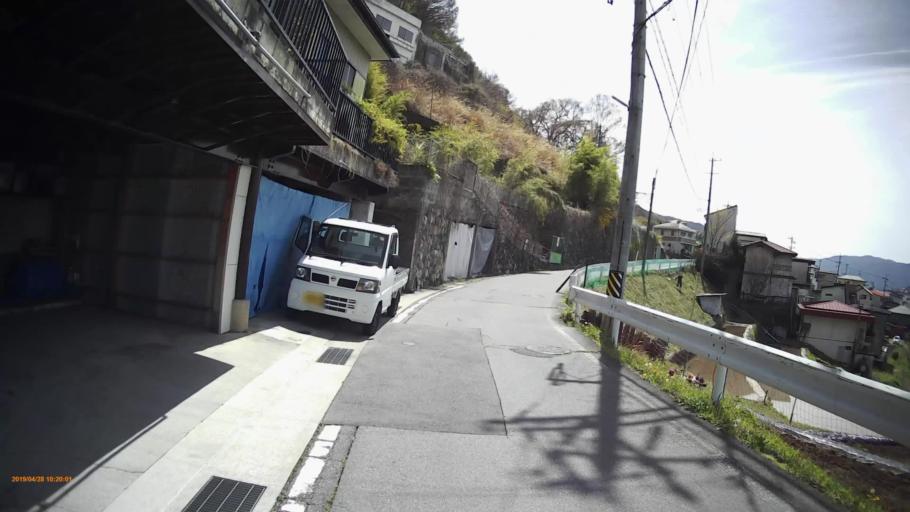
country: JP
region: Nagano
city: Suwa
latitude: 36.0635
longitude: 138.1112
